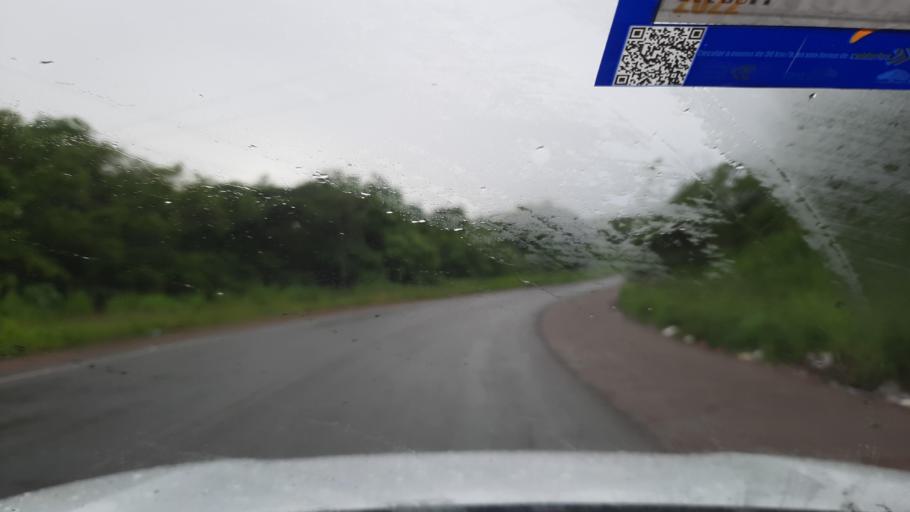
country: NI
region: Rivas
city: Cardenas
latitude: 11.1856
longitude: -85.6186
